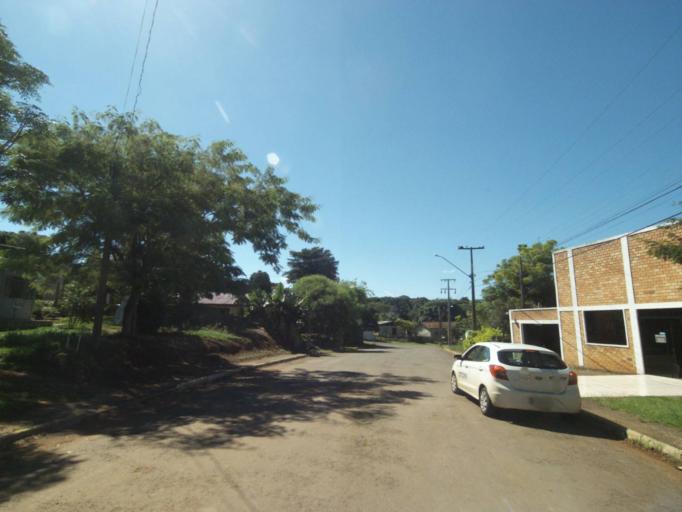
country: BR
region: Parana
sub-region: Pinhao
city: Pinhao
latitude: -25.8362
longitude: -52.0259
